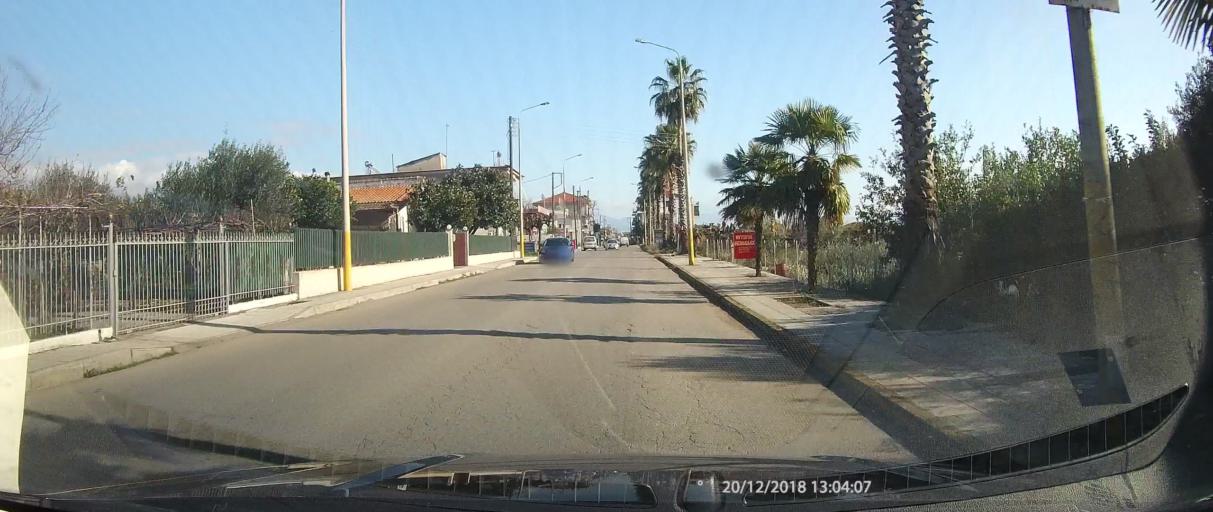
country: GR
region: West Greece
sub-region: Nomos Aitolias kai Akarnanias
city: Panaitolion
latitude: 38.5850
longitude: 21.4306
